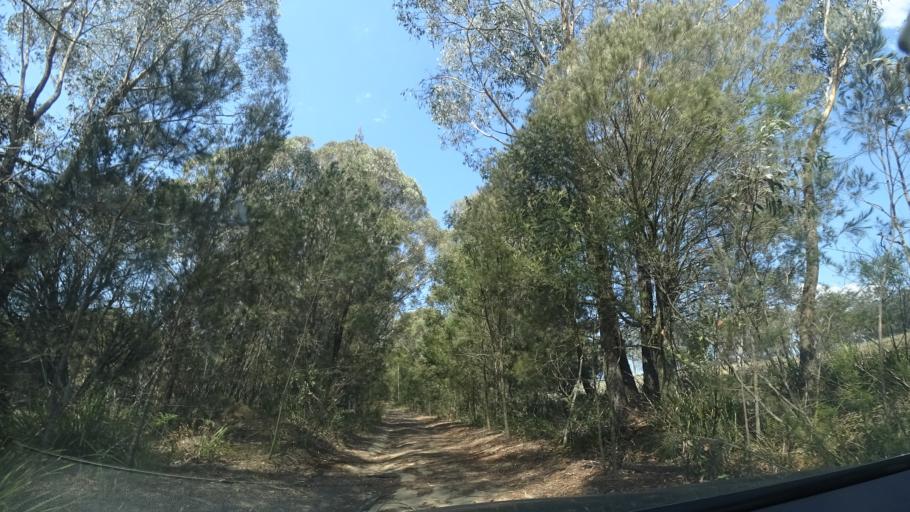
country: AU
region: New South Wales
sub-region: Wingecarribee
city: Bundanoon
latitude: -34.6382
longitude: 150.2470
